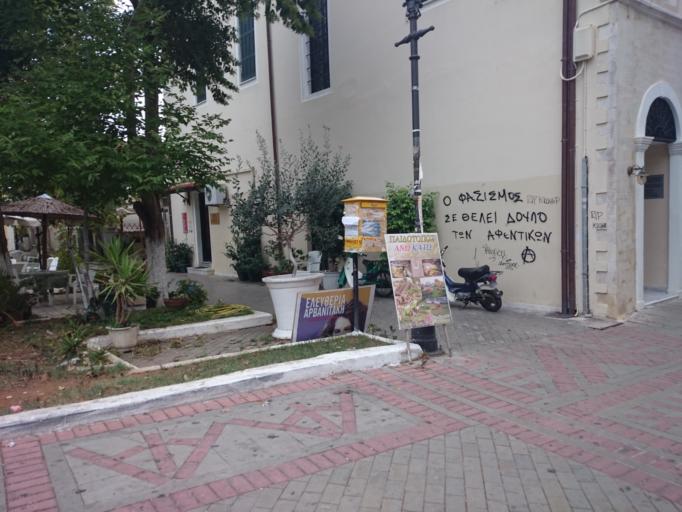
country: GR
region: Epirus
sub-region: Nomos Prevezis
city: Preveza
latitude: 38.9588
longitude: 20.7540
